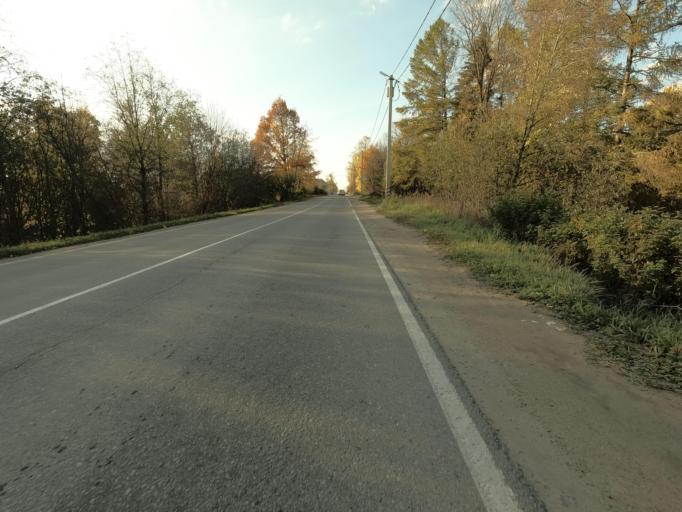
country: RU
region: Leningrad
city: Mga
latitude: 59.7499
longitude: 31.0544
